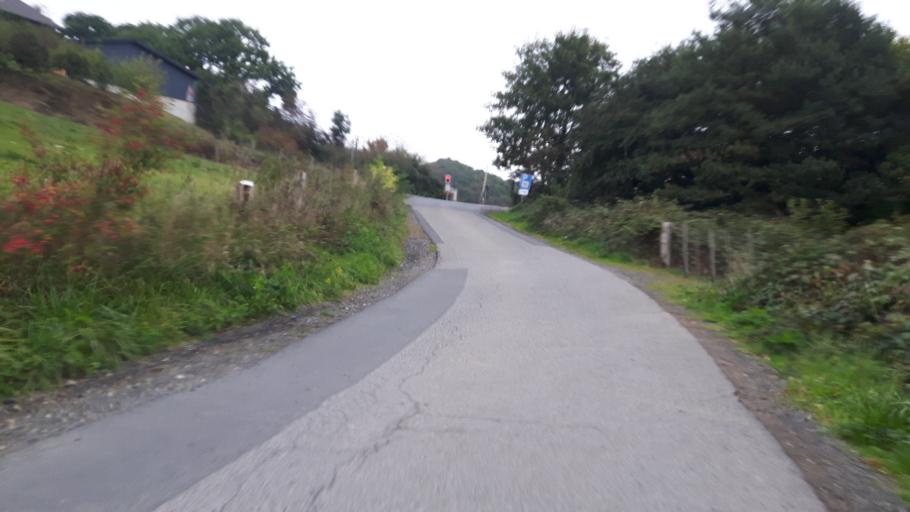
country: DE
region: North Rhine-Westphalia
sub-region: Regierungsbezirk Koln
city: Hennef
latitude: 50.7684
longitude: 7.3585
